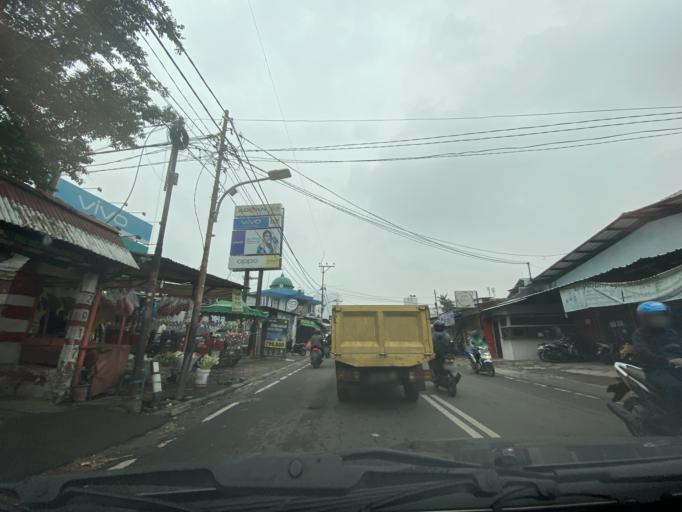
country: ID
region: Jakarta Raya
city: Jakarta
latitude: -6.2052
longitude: 106.7830
